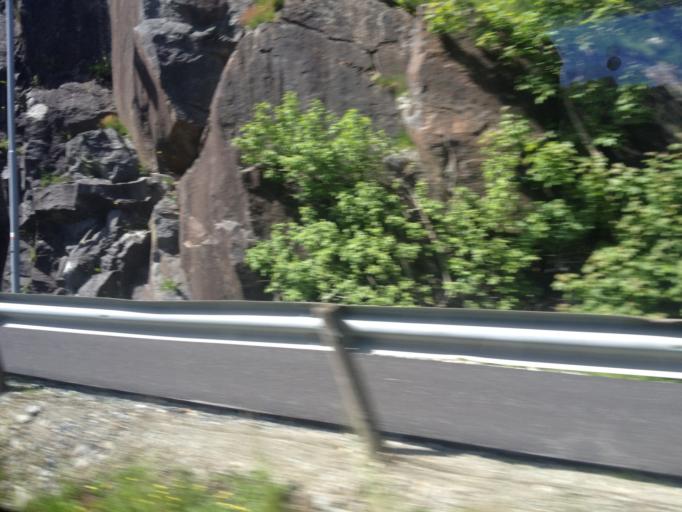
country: NO
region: Rogaland
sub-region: Bjerkreim
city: Vikesa
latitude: 58.5334
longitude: 6.1451
